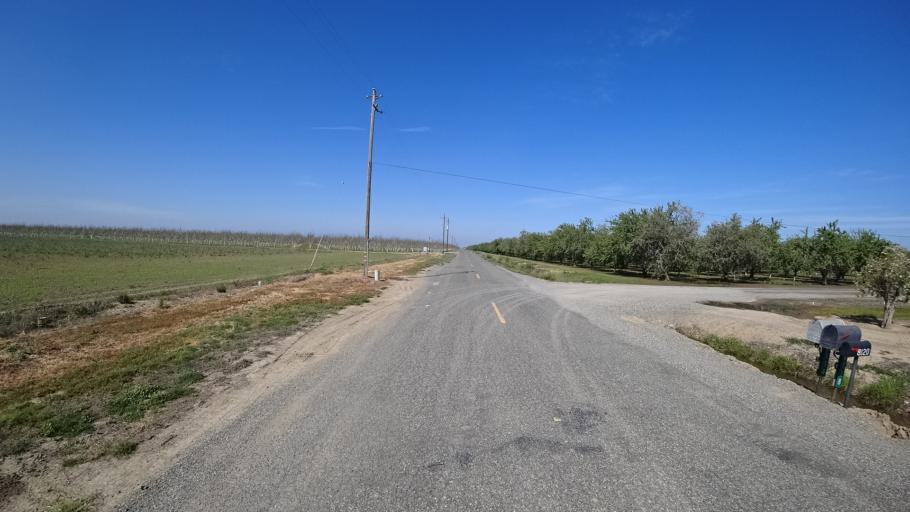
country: US
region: California
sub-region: Glenn County
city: Hamilton City
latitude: 39.6160
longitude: -122.0145
